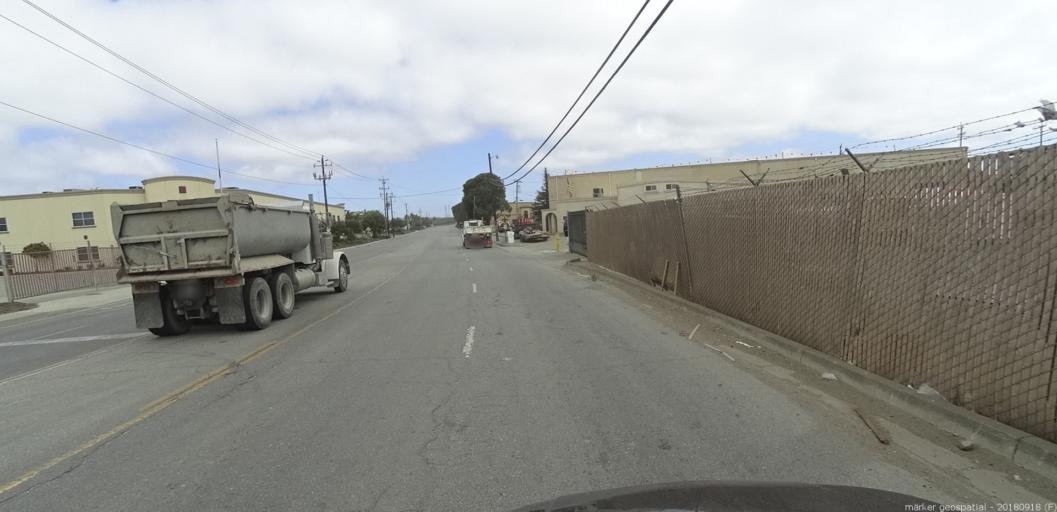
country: US
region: California
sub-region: Monterey County
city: Castroville
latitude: 36.7582
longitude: -121.7433
